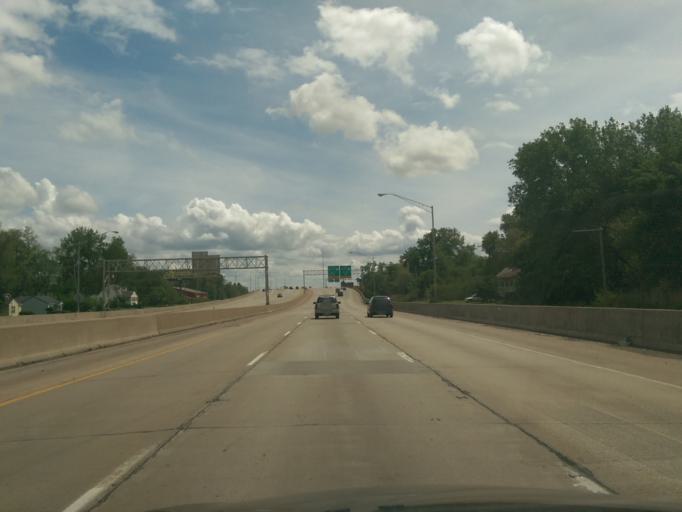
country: US
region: Indiana
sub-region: Lake County
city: Highland
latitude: 41.5796
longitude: -87.4329
